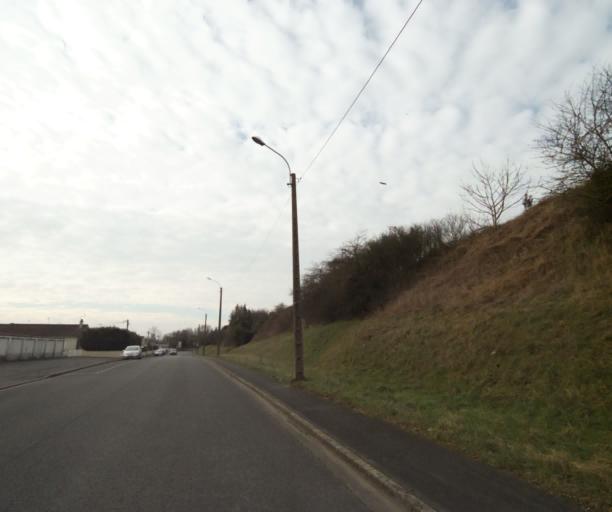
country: FR
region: Poitou-Charentes
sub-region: Departement des Deux-Sevres
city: Niort
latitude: 46.3125
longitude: -0.4593
